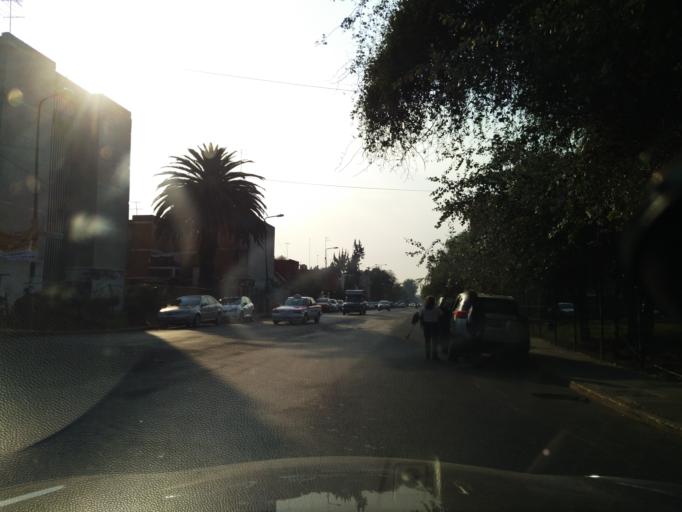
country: MX
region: Mexico City
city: Coyoacan
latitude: 19.3161
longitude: -99.1144
